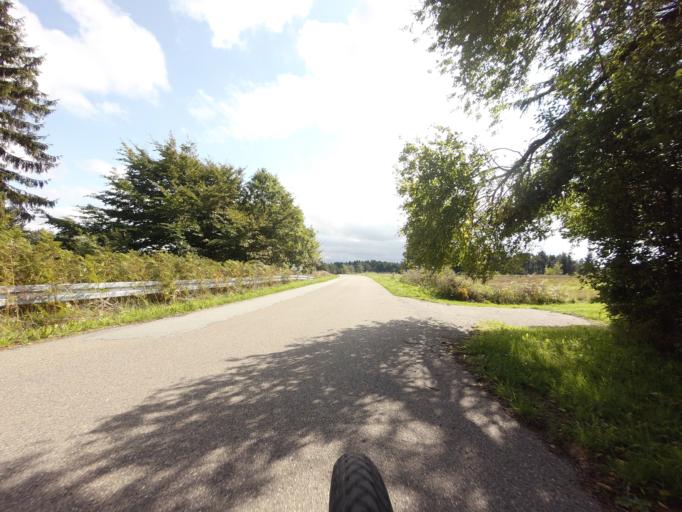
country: DK
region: North Denmark
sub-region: Hjorring Kommune
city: Hirtshals
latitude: 57.5434
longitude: 10.0569
